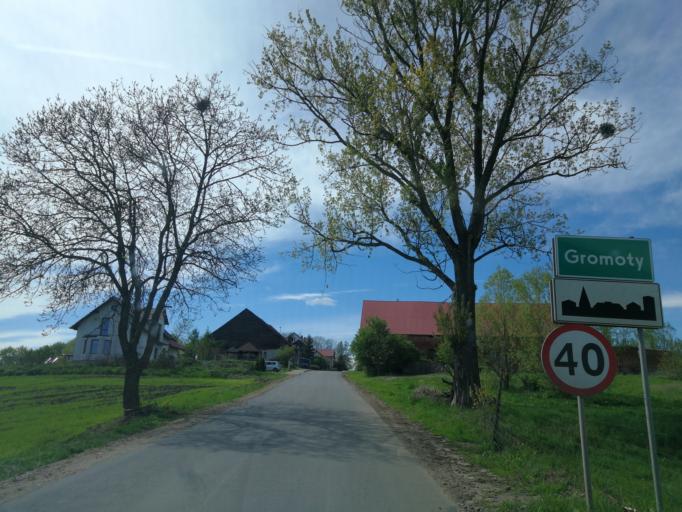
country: PL
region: Warmian-Masurian Voivodeship
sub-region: Powiat ilawski
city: Lubawa
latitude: 53.5976
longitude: 19.7052
